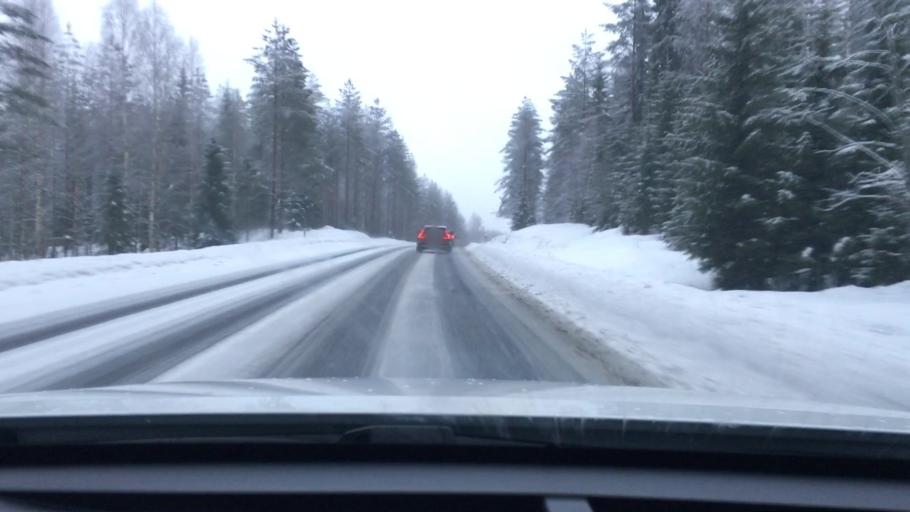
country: FI
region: Northern Savo
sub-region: Ylae-Savo
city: Sonkajaervi
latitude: 63.7667
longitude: 27.4127
